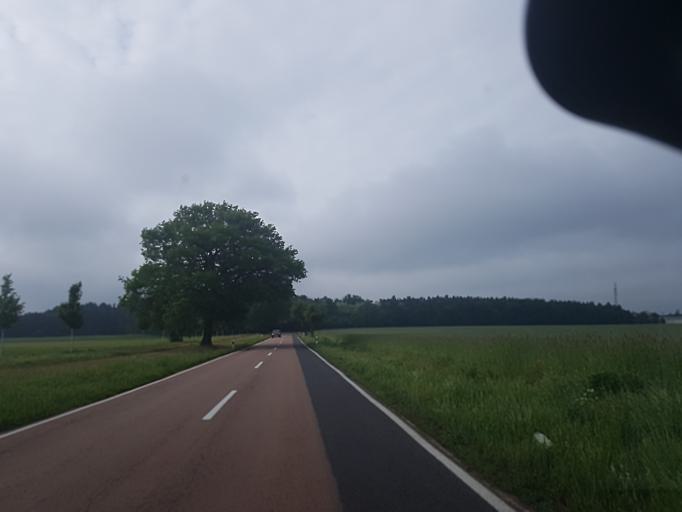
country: DE
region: Saxony-Anhalt
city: Klieken
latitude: 51.9764
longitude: 12.3482
